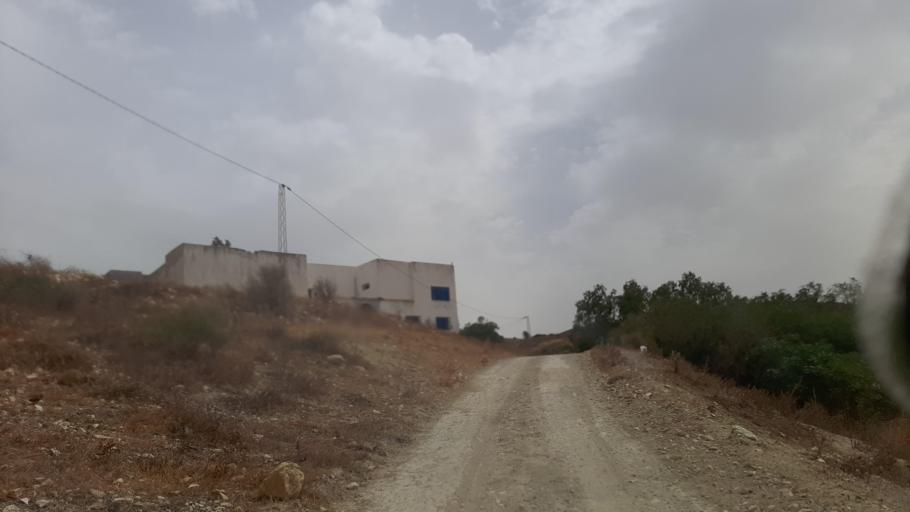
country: TN
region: Tunis
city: La Mohammedia
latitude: 36.5691
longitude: 10.1386
